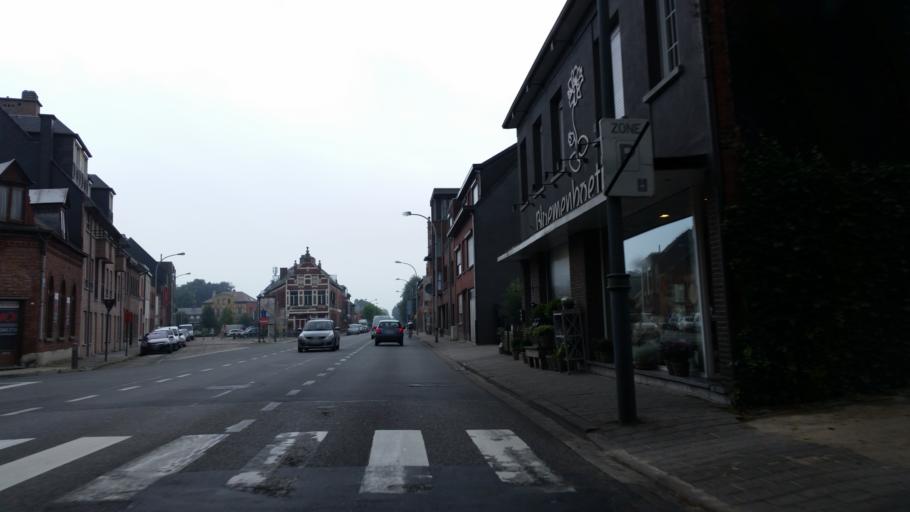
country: BE
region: Flanders
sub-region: Provincie Antwerpen
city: Hoogstraten
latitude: 51.4070
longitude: 4.7633
